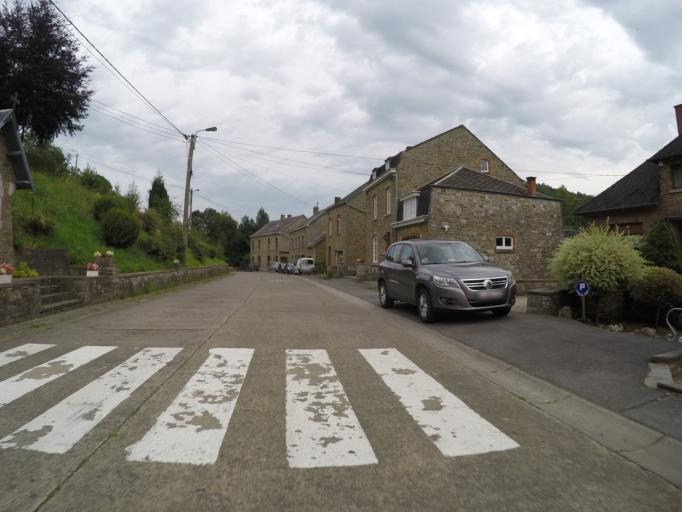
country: BE
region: Wallonia
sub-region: Province de Namur
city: Assesse
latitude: 50.3238
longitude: 5.0030
